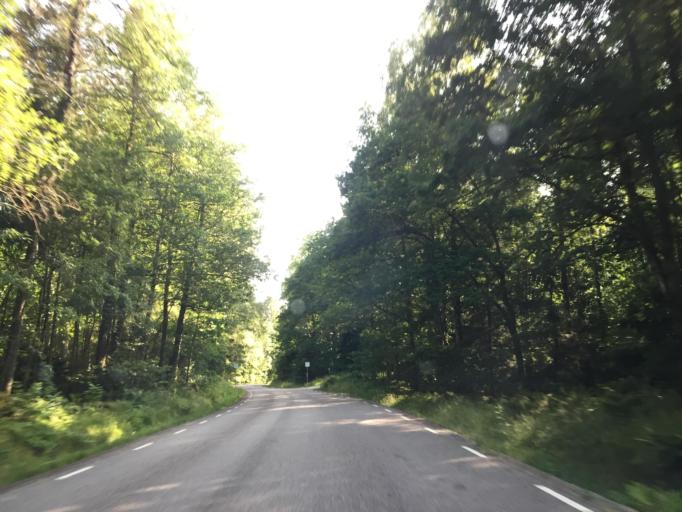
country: SE
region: Vaestra Goetaland
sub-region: Trollhattan
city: Trollhattan
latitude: 58.2646
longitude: 12.2331
